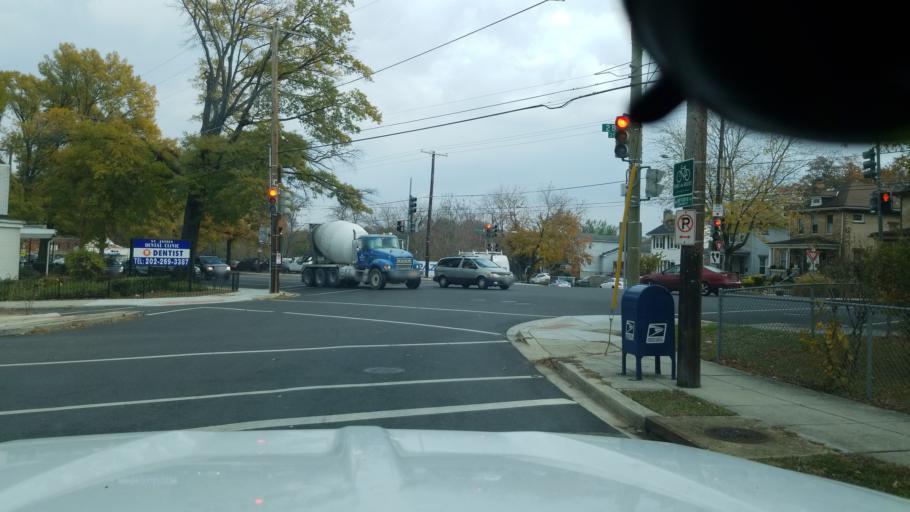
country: US
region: Maryland
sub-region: Prince George's County
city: Mount Rainier
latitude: 38.9331
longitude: -76.9687
